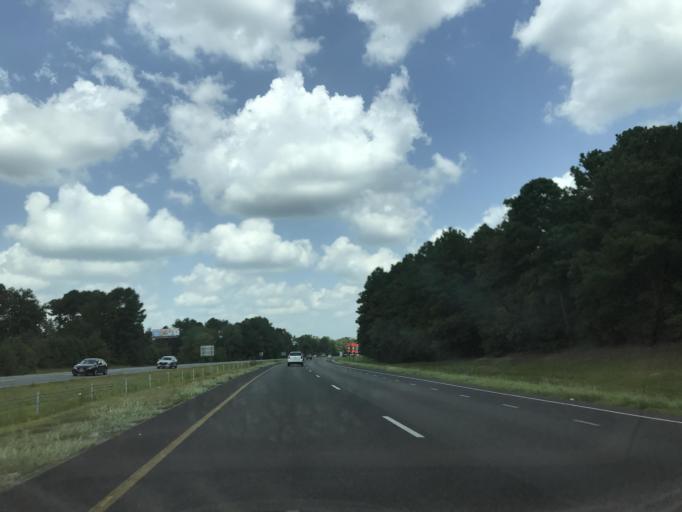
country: US
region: North Carolina
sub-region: Duplin County
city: Rose Hill
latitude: 34.8267
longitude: -77.9978
